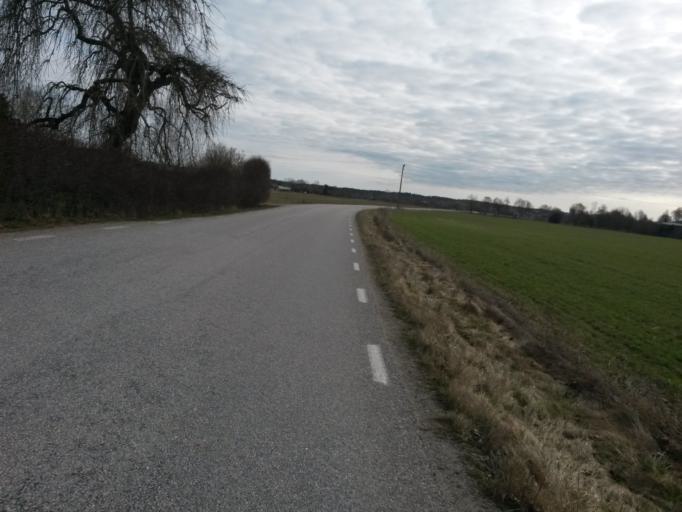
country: SE
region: Vaestra Goetaland
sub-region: Herrljunga Kommun
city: Herrljunga
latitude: 58.0908
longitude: 12.9949
